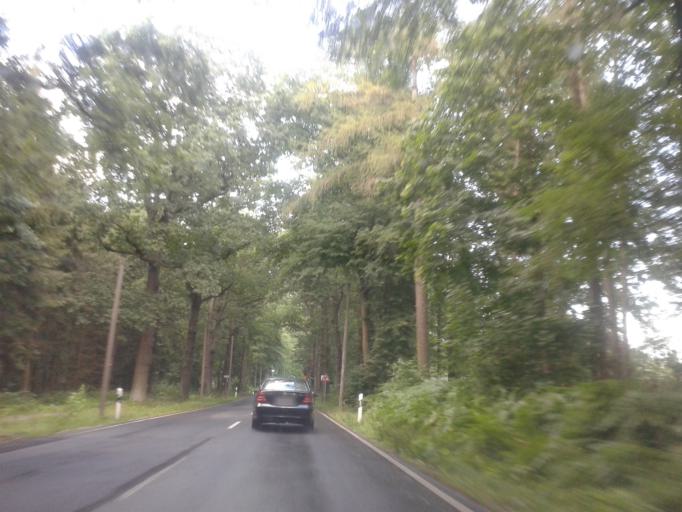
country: DE
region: Saxony
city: Radeberg
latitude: 51.0730
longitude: 13.8812
